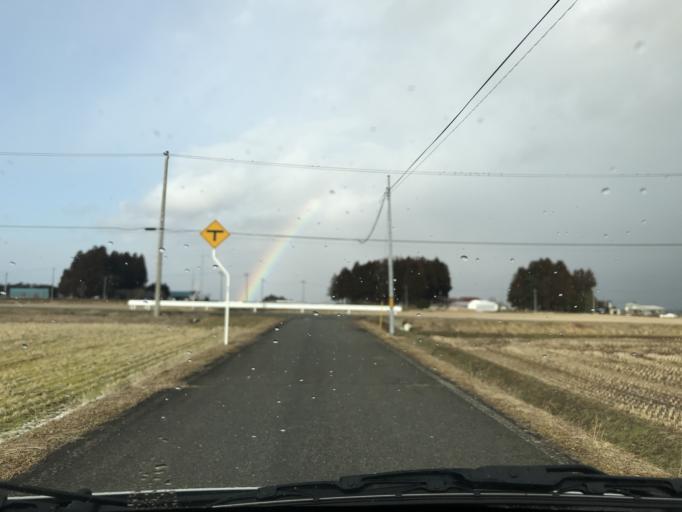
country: JP
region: Iwate
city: Mizusawa
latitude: 39.0923
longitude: 141.0302
